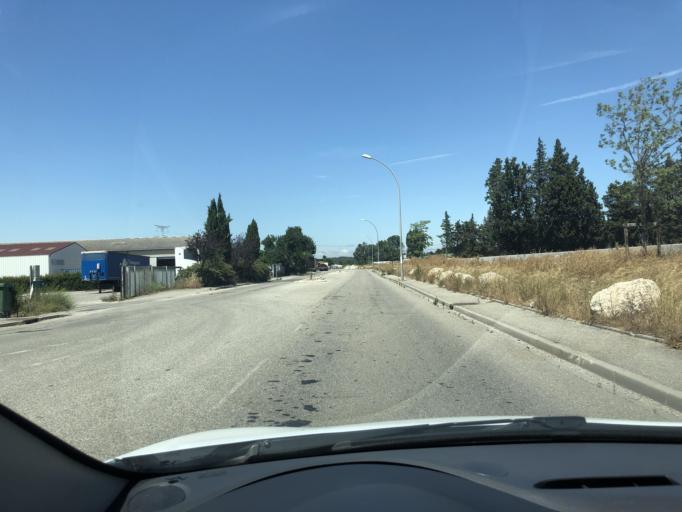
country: FR
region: Provence-Alpes-Cote d'Azur
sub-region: Departement des Bouches-du-Rhone
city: Noves
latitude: 43.8949
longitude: 4.8804
